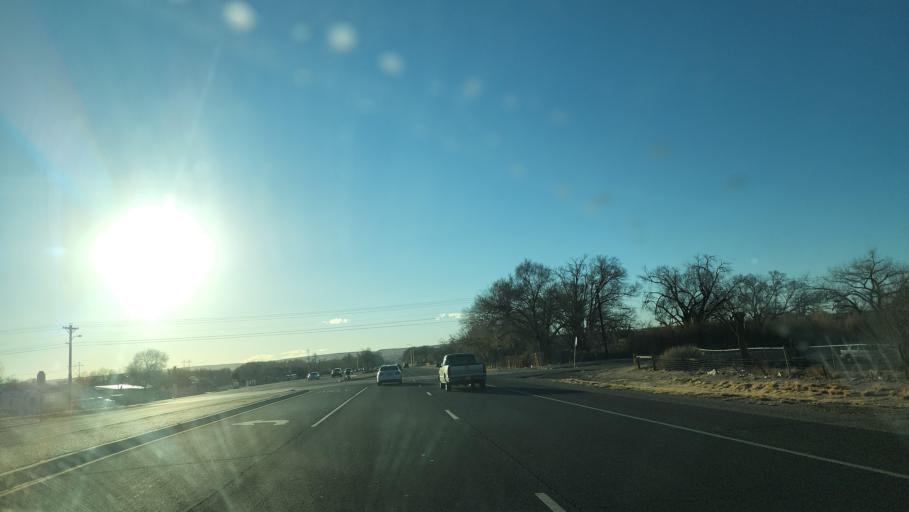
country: US
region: New Mexico
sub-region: Bernalillo County
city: South Valley
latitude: 35.0269
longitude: -106.6846
